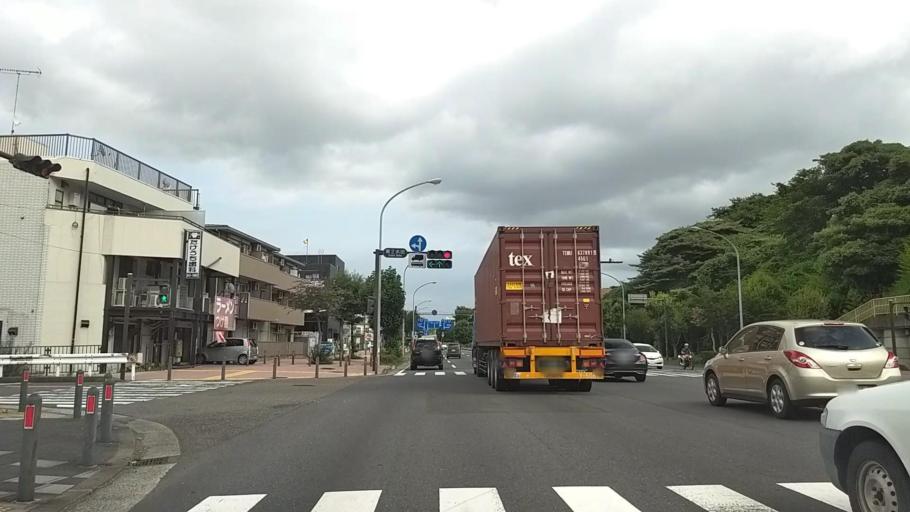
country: JP
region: Kanagawa
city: Yokohama
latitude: 35.4078
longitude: 139.5651
